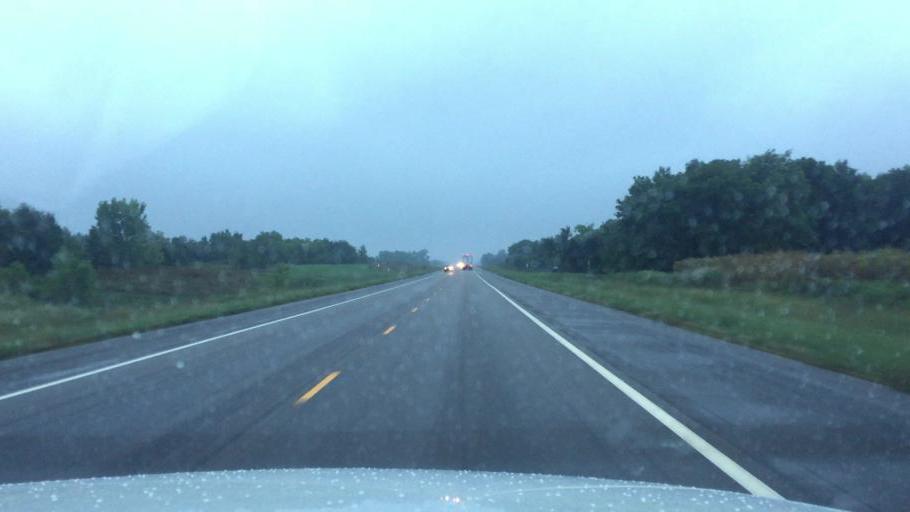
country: US
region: Kansas
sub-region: Montgomery County
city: Cherryvale
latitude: 37.4361
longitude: -95.4878
